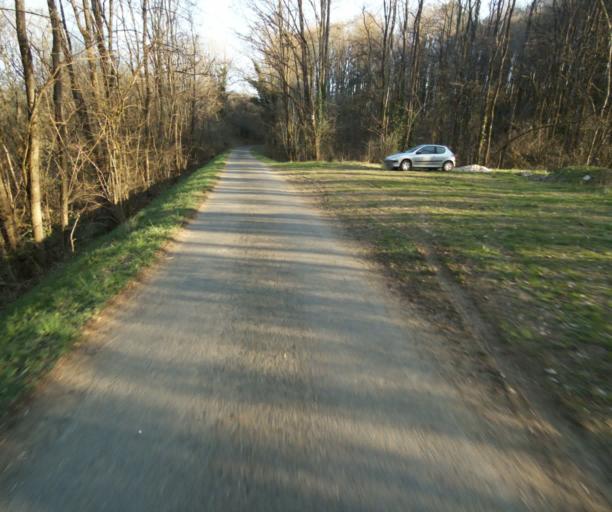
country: FR
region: Limousin
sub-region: Departement de la Correze
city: Saint-Clement
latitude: 45.3508
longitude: 1.6702
